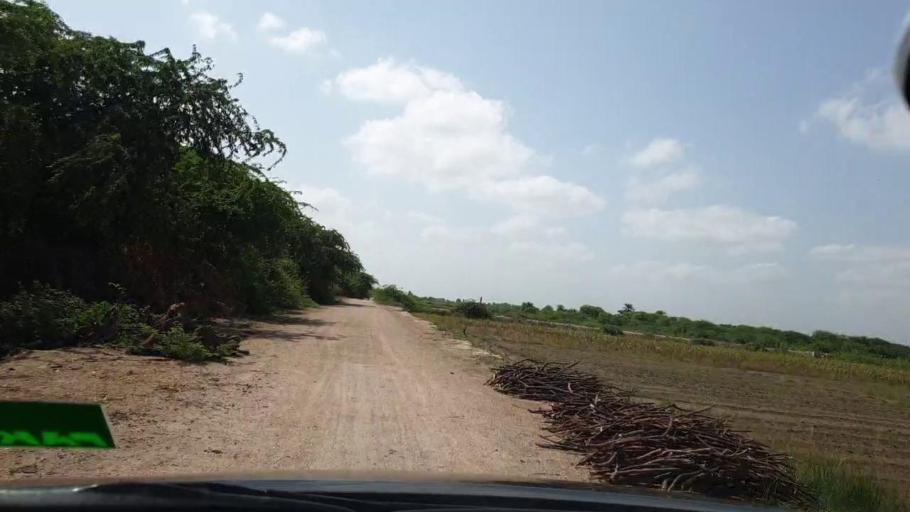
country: PK
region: Sindh
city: Kadhan
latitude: 24.5782
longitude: 69.1513
